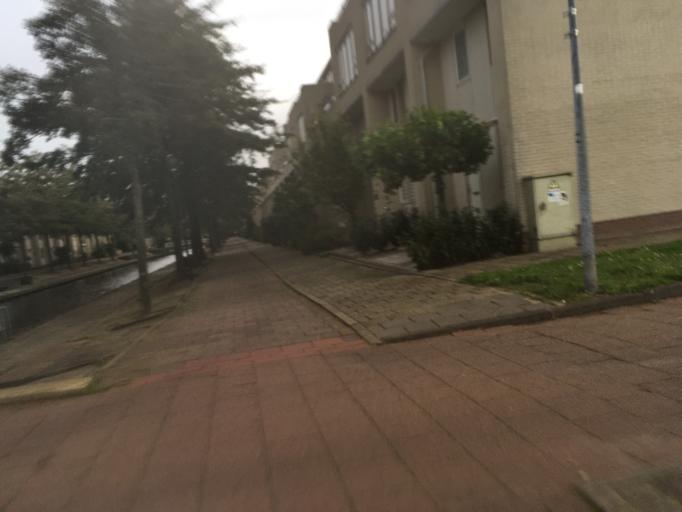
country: NL
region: North Holland
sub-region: Gemeente Haarlem
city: Haarlem
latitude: 52.3782
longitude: 4.6694
